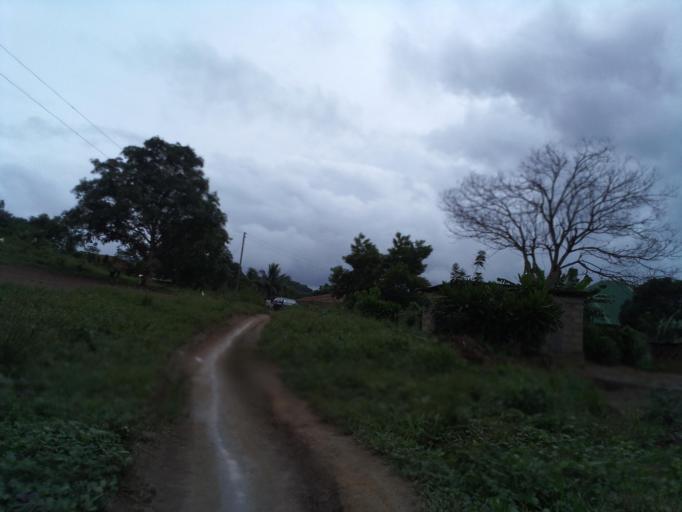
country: SL
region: Eastern Province
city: Kenema
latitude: 7.8791
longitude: -11.1638
